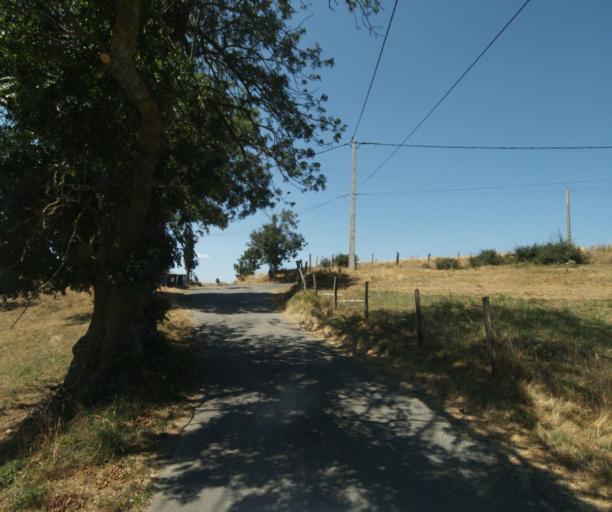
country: FR
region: Rhone-Alpes
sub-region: Departement du Rhone
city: Courzieu
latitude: 45.7258
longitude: 4.5493
